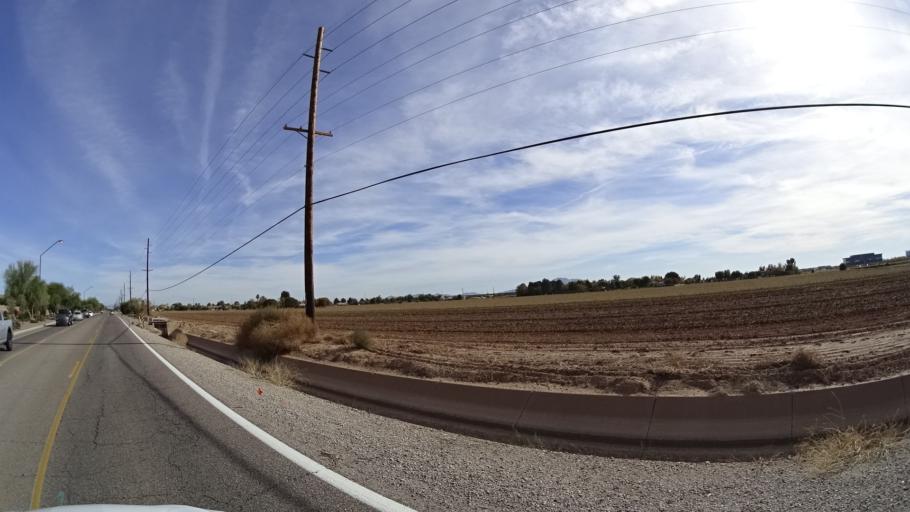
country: US
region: Arizona
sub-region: Maricopa County
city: Gilbert
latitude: 33.2918
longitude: -111.7808
